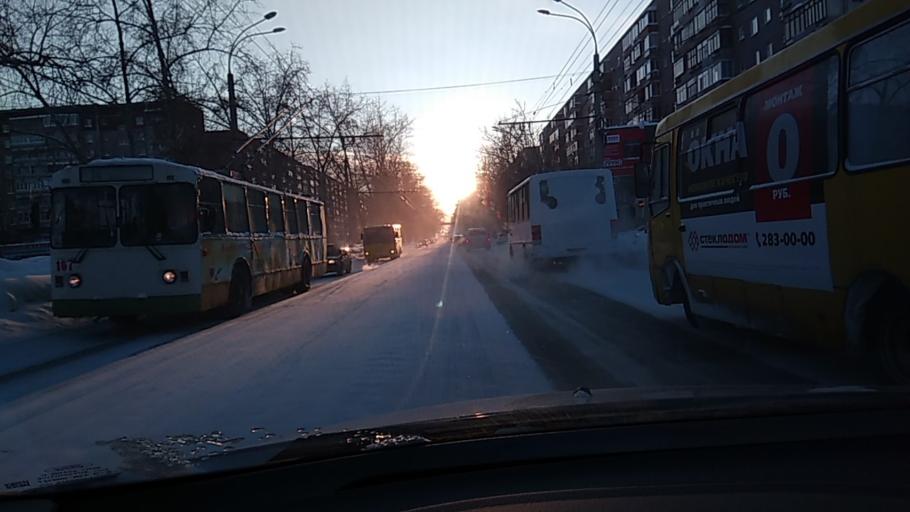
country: RU
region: Sverdlovsk
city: Sovkhoznyy
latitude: 56.7965
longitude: 60.5791
